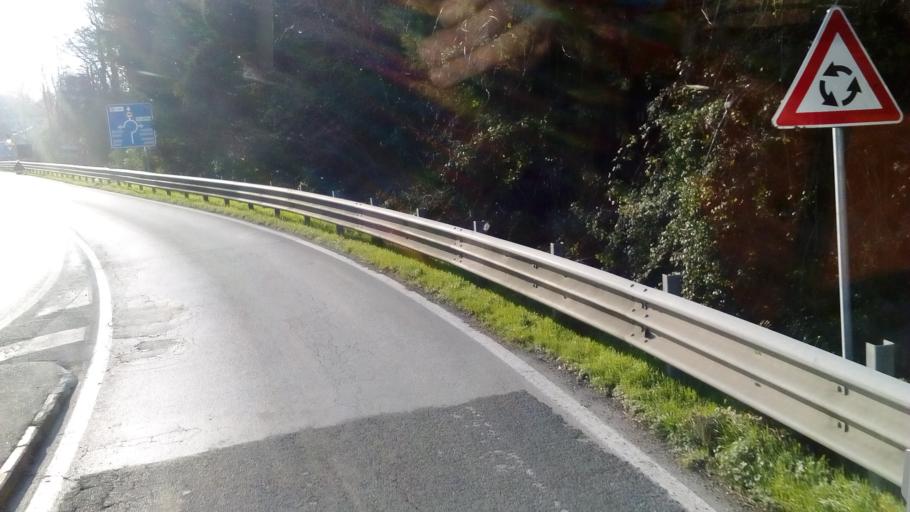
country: IT
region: Friuli Venezia Giulia
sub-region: Provincia di Udine
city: San Giorgio di Nogaro
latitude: 45.8351
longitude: 13.2123
